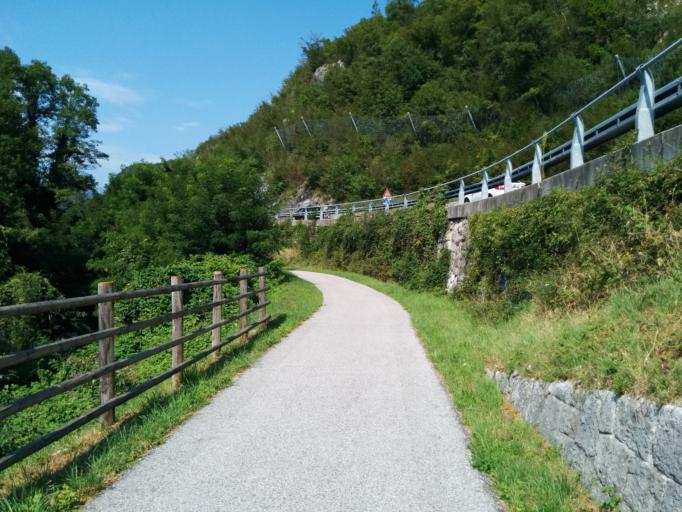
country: IT
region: Friuli Venezia Giulia
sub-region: Provincia di Udine
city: Villa Santina
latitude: 46.4220
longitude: 12.9088
